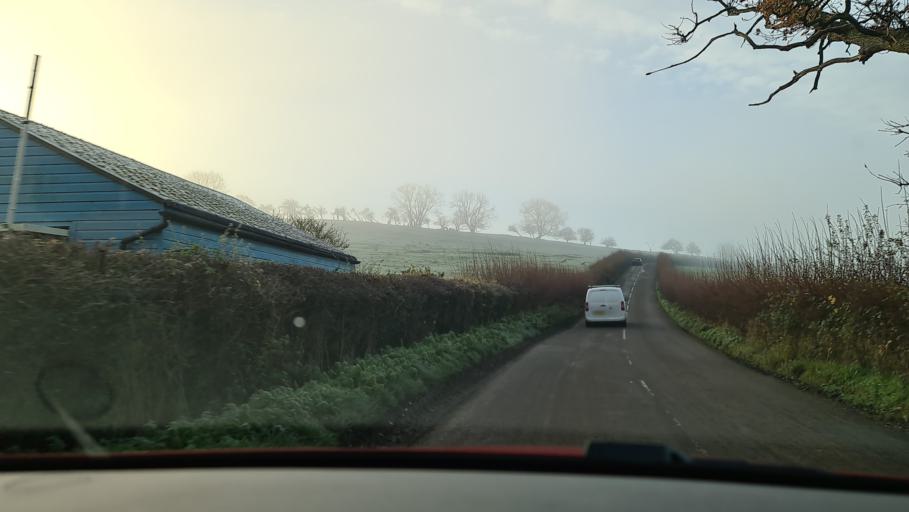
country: GB
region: England
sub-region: Buckinghamshire
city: Waddesdon
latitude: 51.8323
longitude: -0.9574
